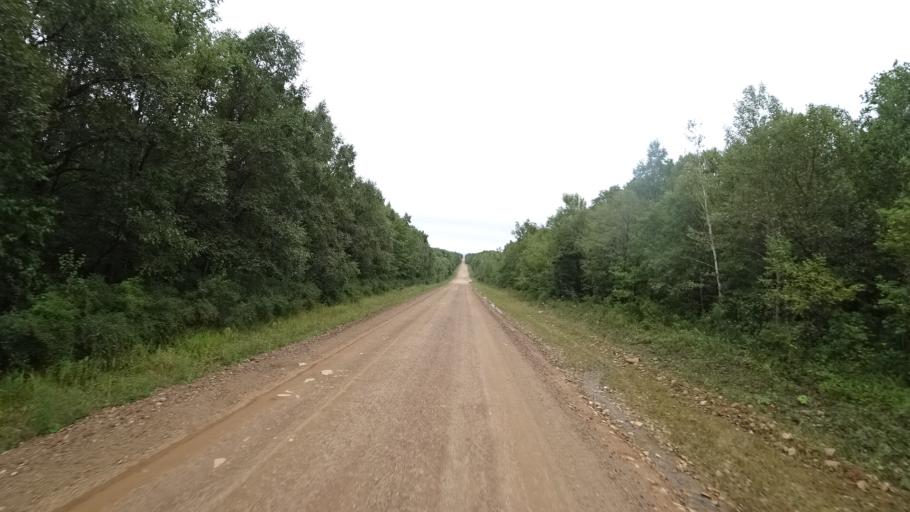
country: RU
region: Primorskiy
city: Ivanovka
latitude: 44.0358
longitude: 132.5346
